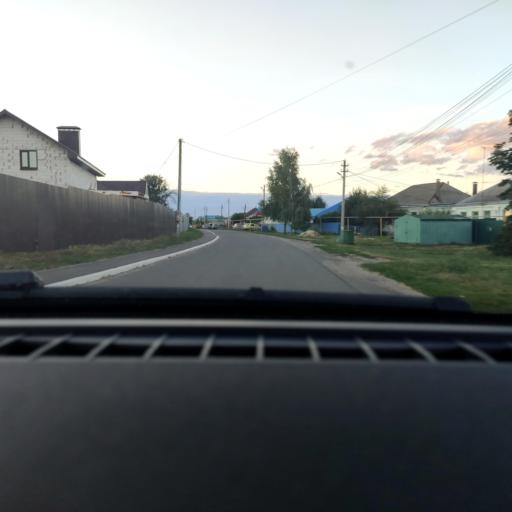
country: RU
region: Voronezj
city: Novaya Usman'
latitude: 51.6612
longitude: 39.3420
